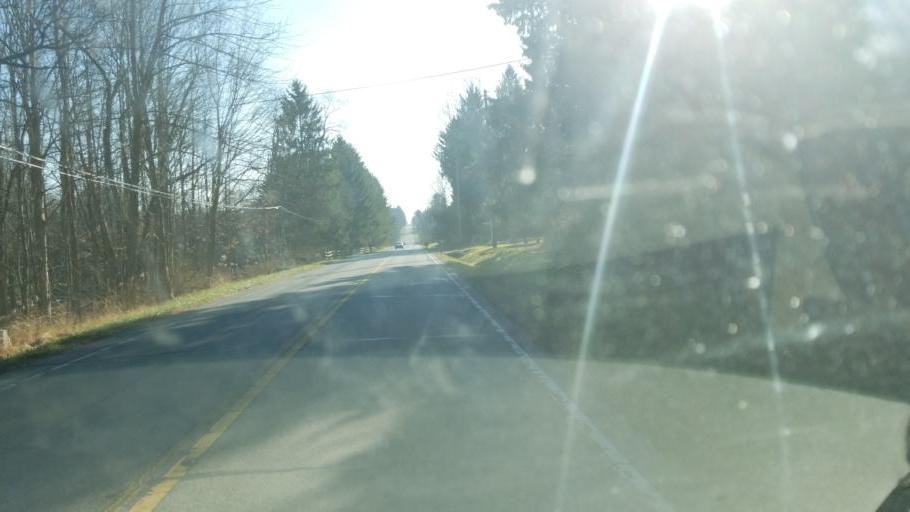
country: US
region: Ohio
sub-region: Geauga County
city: Bainbridge
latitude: 41.3953
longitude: -81.2464
